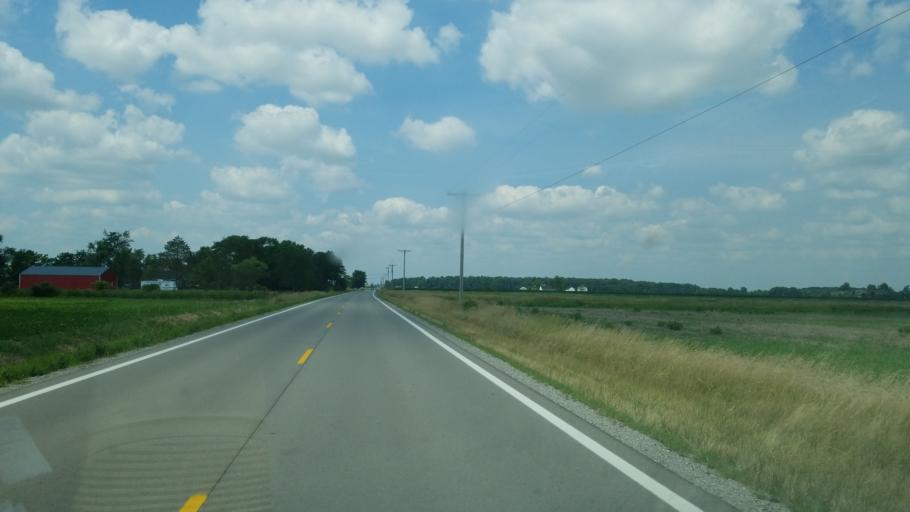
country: US
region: Ohio
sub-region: Henry County
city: Holgate
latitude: 41.2822
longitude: -84.1803
